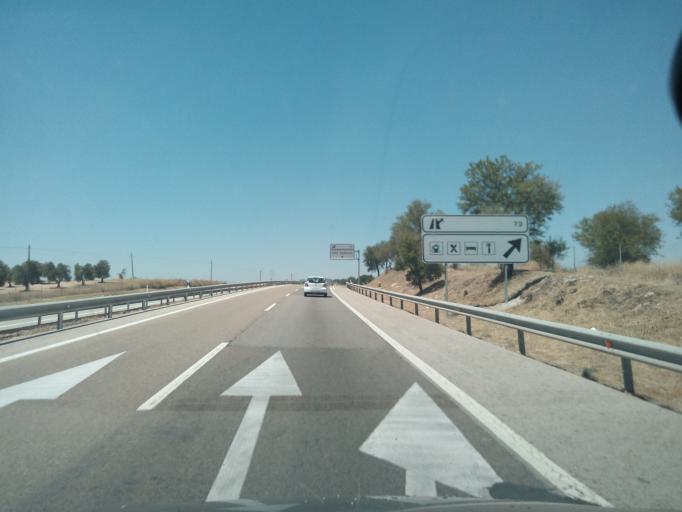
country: ES
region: Castille-La Mancha
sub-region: Province of Toledo
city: Dosbarrios
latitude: 39.8634
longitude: -3.4767
